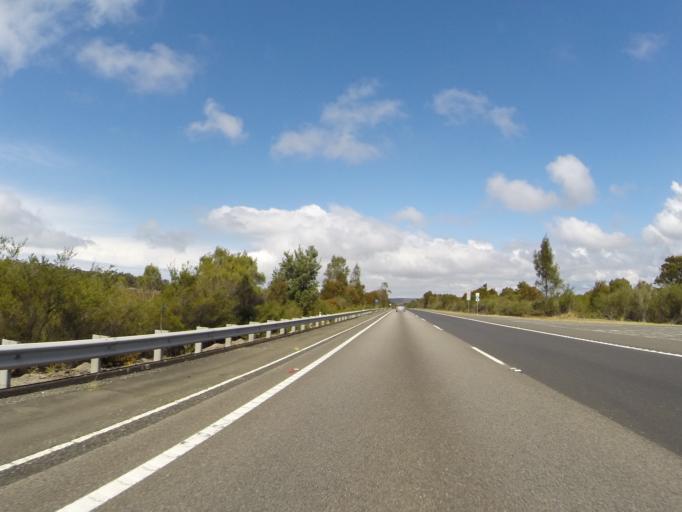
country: AU
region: New South Wales
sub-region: Wollongong
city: Bulli
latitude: -34.2611
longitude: 150.9297
